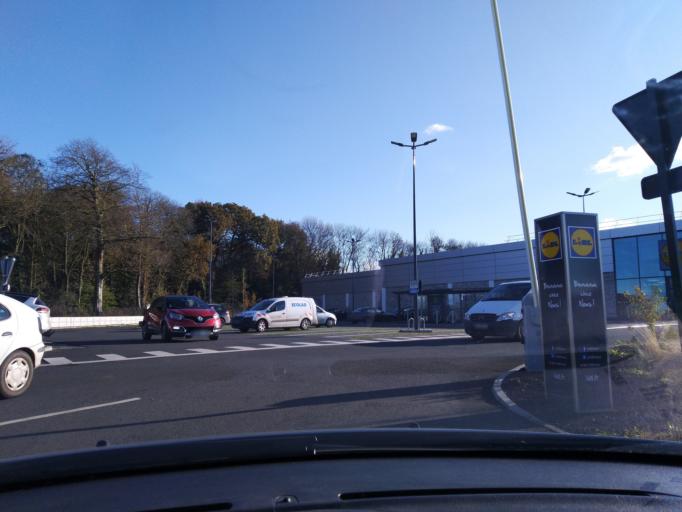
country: FR
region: Brittany
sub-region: Departement des Cotes-d'Armor
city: Plestin-les-Greves
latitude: 48.6622
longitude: -3.6255
